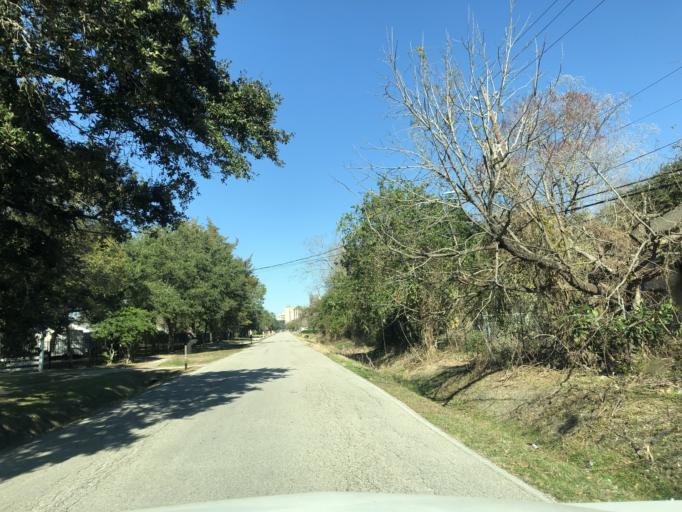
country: US
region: Texas
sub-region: Fort Bend County
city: Missouri City
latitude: 29.6813
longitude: -95.5217
